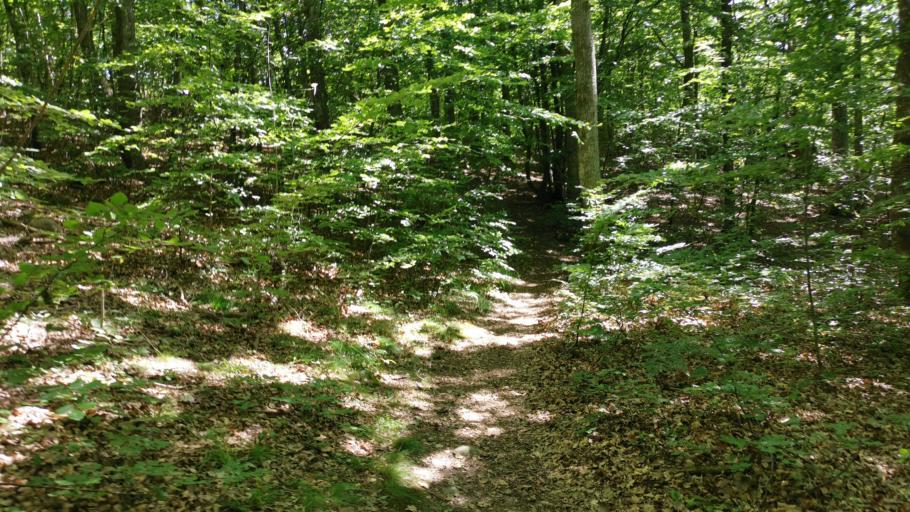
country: SE
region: Vaestra Goetaland
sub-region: Lysekils Kommun
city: Lysekil
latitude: 58.2399
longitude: 11.4839
